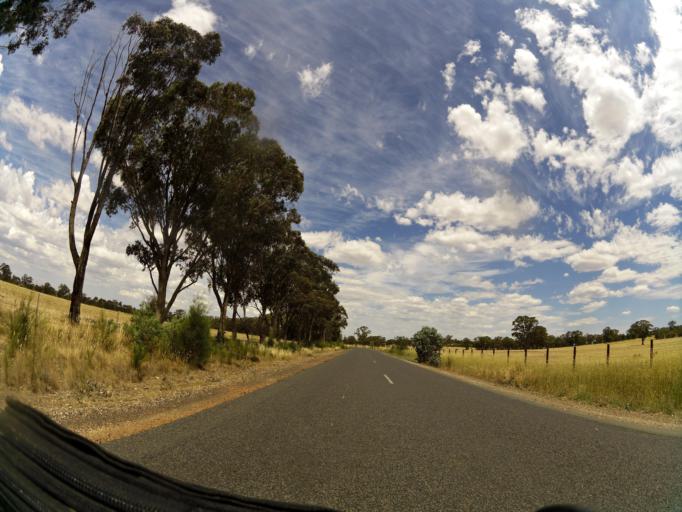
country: AU
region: Victoria
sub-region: Campaspe
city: Kyabram
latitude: -36.7784
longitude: 145.1123
